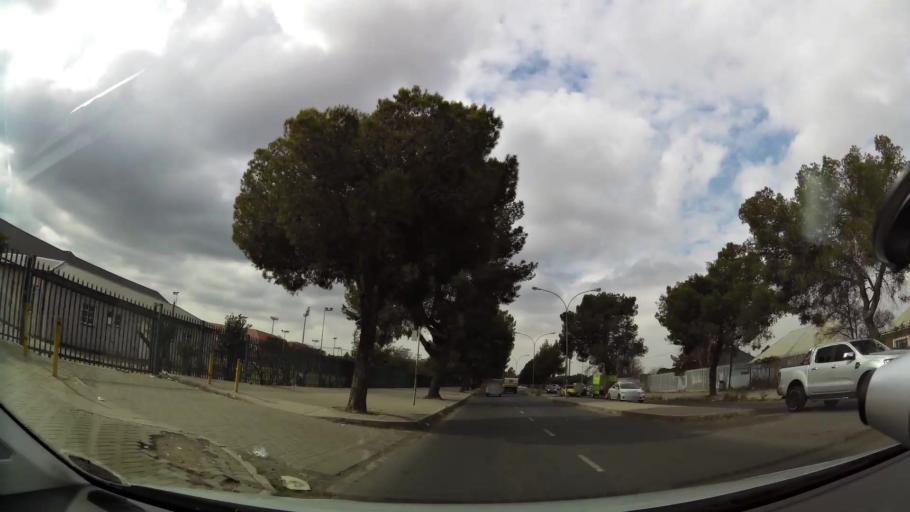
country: ZA
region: Orange Free State
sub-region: Mangaung Metropolitan Municipality
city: Bloemfontein
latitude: -29.1242
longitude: 26.2130
